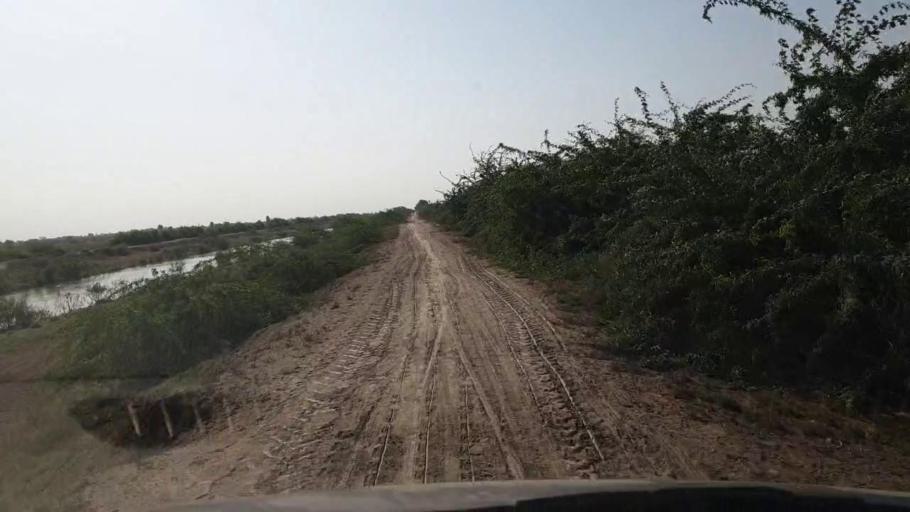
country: PK
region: Sindh
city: Kadhan
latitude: 24.5915
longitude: 69.0764
